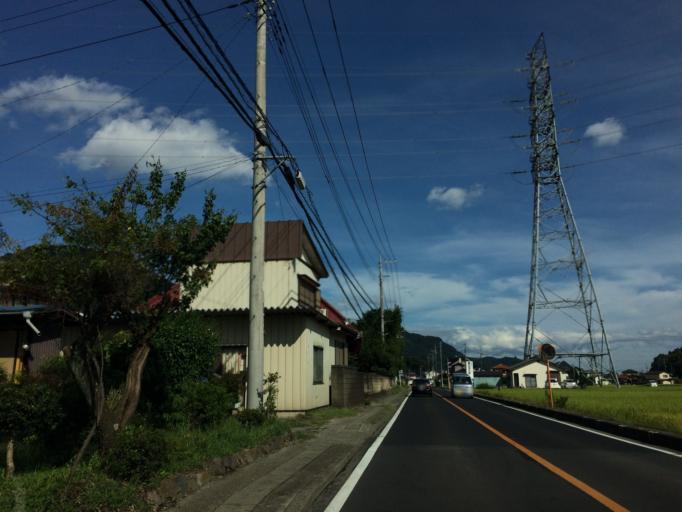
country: JP
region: Gunma
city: Nakanojomachi
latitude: 36.5728
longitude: 138.8623
